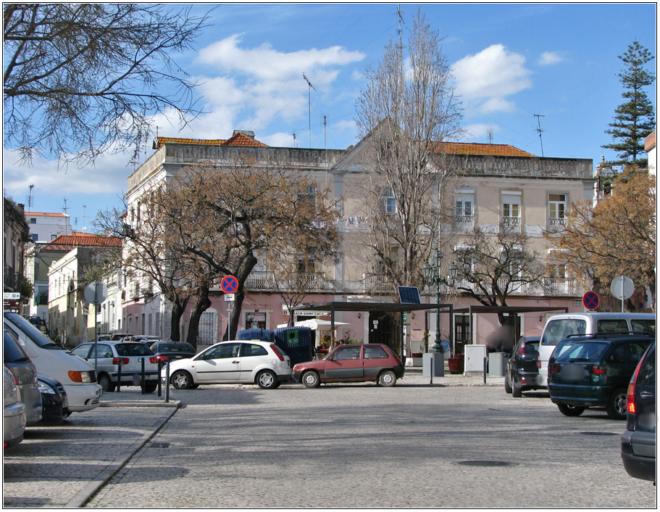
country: PT
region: Setubal
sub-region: Setubal
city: Setubal
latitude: 38.5238
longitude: -8.8992
